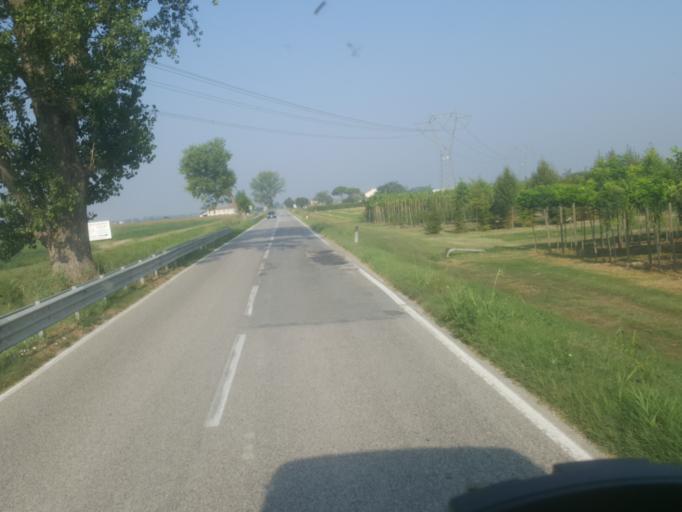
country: IT
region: Emilia-Romagna
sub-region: Provincia di Ravenna
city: Voltana
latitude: 44.5567
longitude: 11.9272
